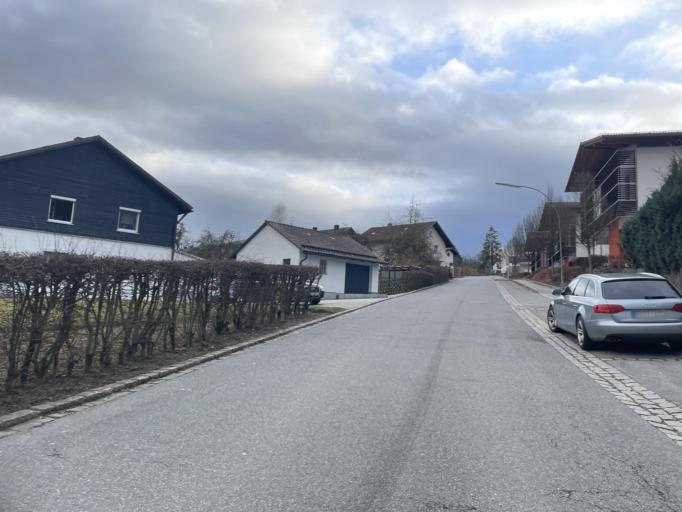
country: DE
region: Bavaria
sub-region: Lower Bavaria
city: Viechtach
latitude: 49.0740
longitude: 12.8881
